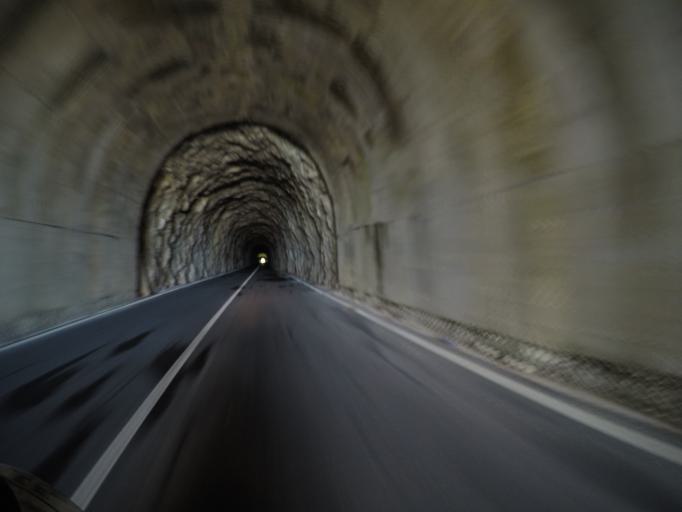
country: IT
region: Tuscany
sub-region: Provincia di Massa-Carrara
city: Montignoso
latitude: 44.0655
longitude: 10.2254
